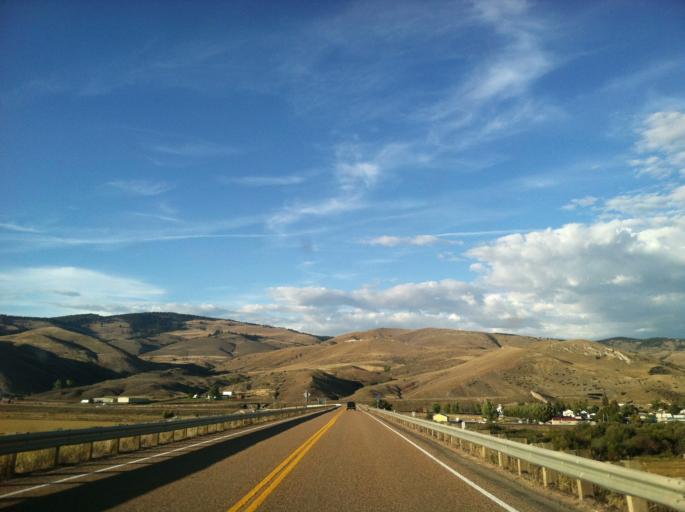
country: US
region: Montana
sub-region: Granite County
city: Philipsburg
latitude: 46.6665
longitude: -113.1549
